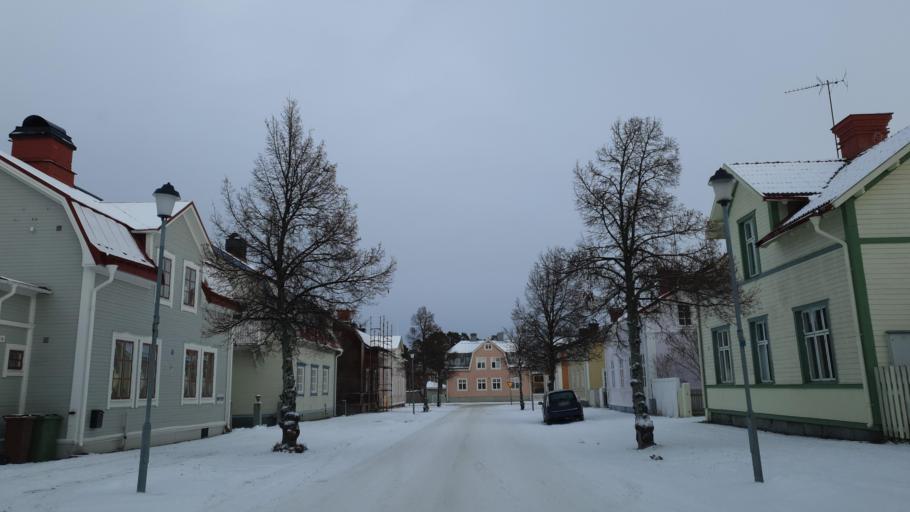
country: SE
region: Gaevleborg
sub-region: Soderhamns Kommun
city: Soderhamn
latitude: 61.3065
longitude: 17.0508
